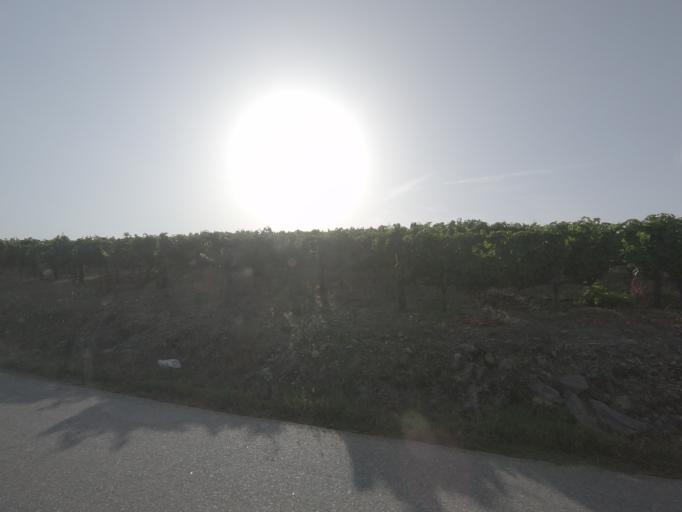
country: PT
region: Vila Real
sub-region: Sabrosa
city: Sabrosa
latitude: 41.2378
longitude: -7.4702
